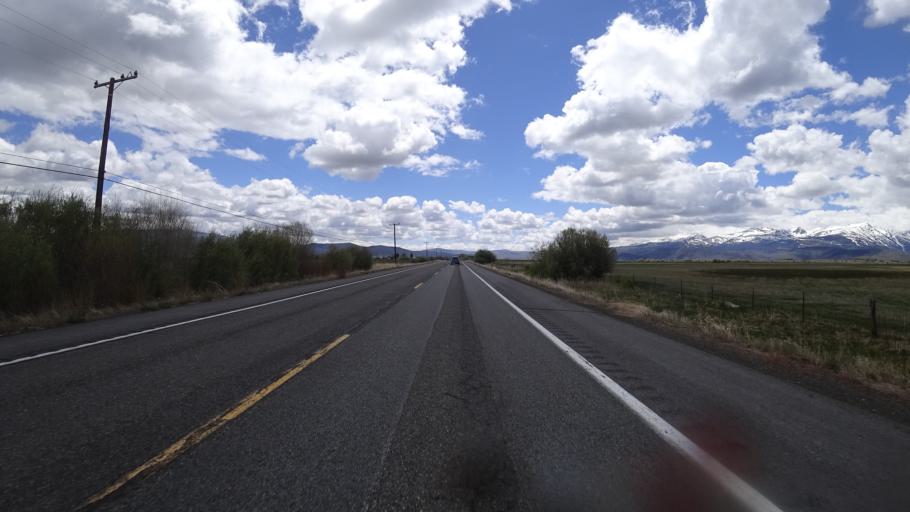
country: US
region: California
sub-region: Mono County
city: Bridgeport
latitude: 38.2671
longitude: -119.2805
